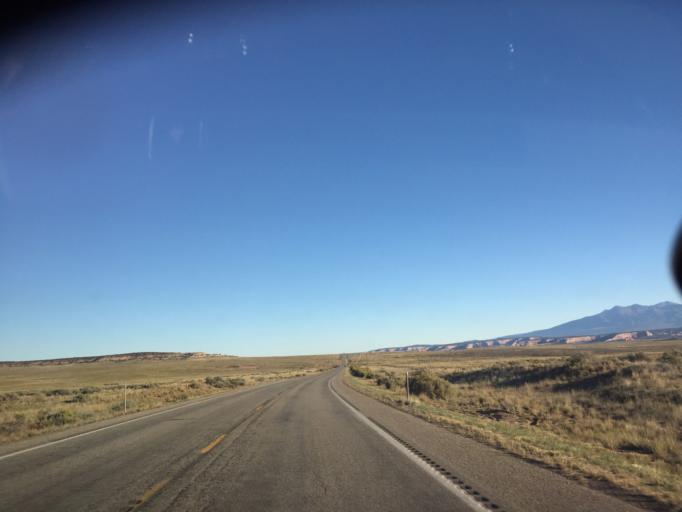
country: US
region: Utah
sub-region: San Juan County
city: Monticello
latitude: 38.1073
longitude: -109.3633
